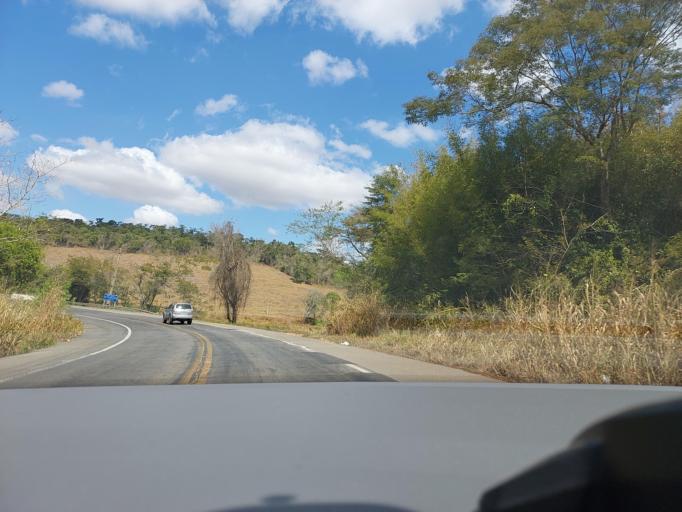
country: BR
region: Minas Gerais
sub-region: Muriae
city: Muriae
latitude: -21.1450
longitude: -42.1691
